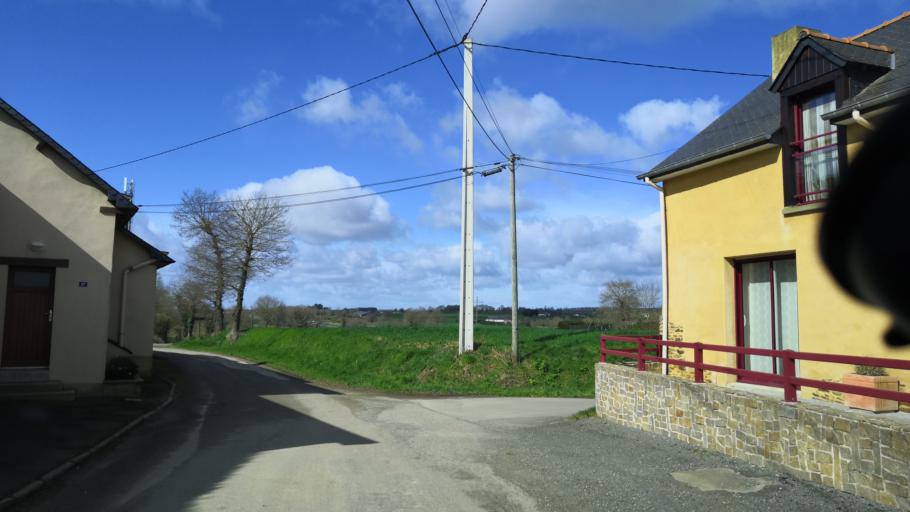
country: FR
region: Brittany
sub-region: Departement d'Ille-et-Vilaine
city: Bedee
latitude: 48.1852
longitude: -1.9741
